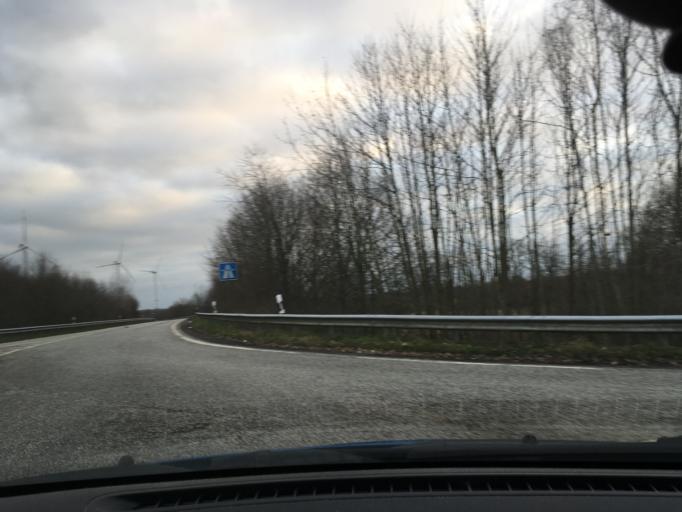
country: DE
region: Schleswig-Holstein
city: Tensbuttel-Rost
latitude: 54.1160
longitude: 9.2570
